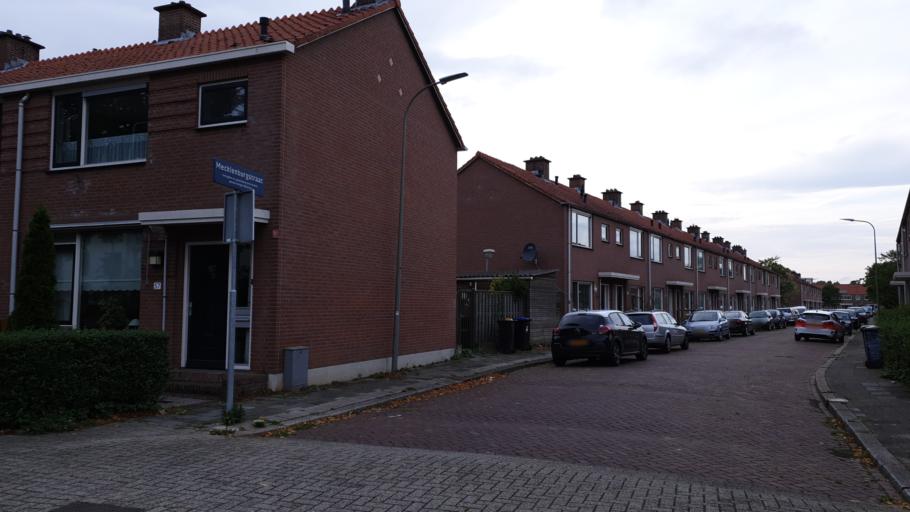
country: NL
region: South Holland
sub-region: Gemeente Dordrecht
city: Dordrecht
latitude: 51.7998
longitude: 4.6681
